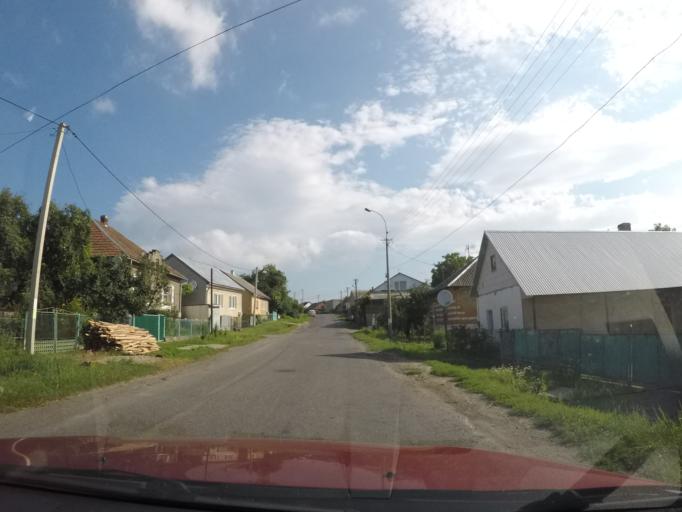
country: UA
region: Zakarpattia
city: Velykyi Bereznyi
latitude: 48.9109
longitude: 22.4598
